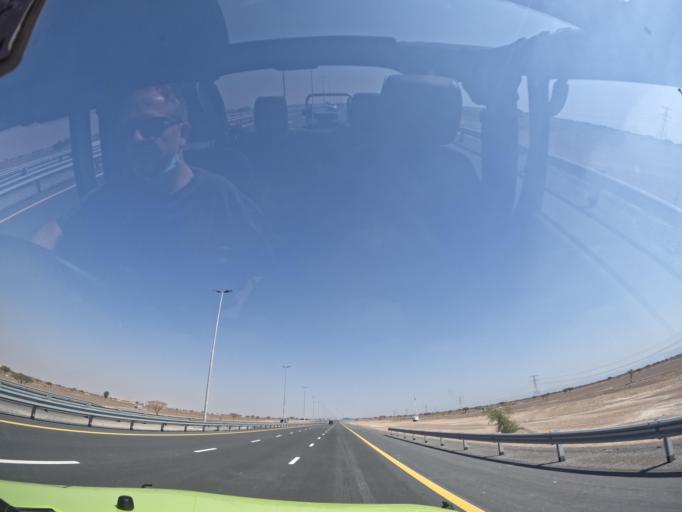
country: AE
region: Ash Shariqah
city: Adh Dhayd
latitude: 24.9481
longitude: 55.8326
